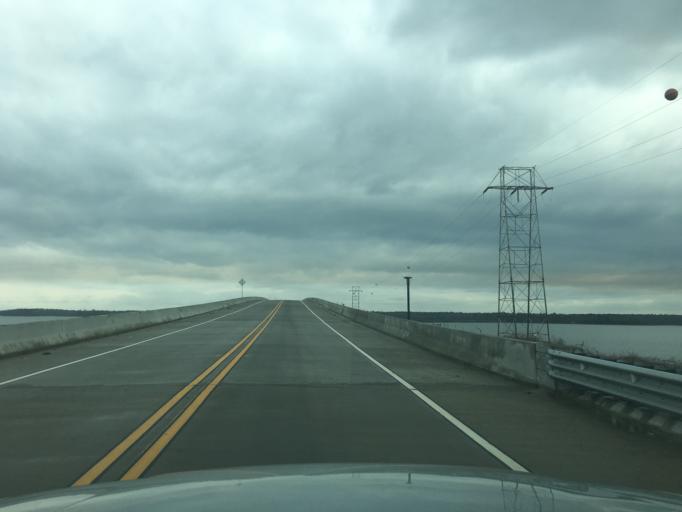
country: US
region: Georgia
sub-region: Columbia County
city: Appling
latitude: 33.6912
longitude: -82.3364
